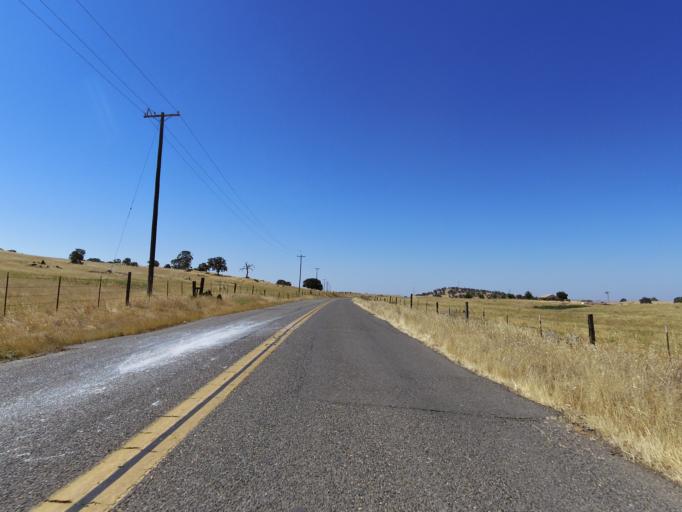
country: US
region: California
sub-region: Merced County
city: Planada
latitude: 37.5889
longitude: -120.3069
